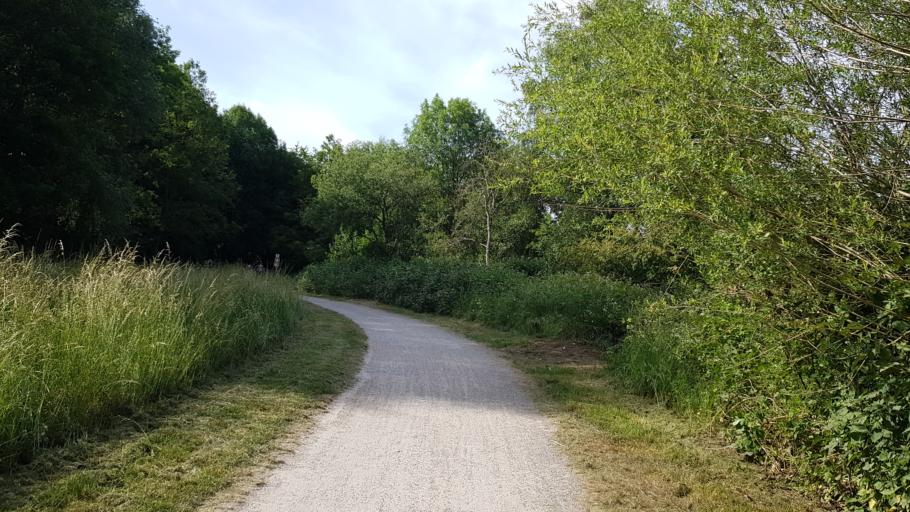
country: DE
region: North Rhine-Westphalia
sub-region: Regierungsbezirk Dusseldorf
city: Muelheim (Ruhr)
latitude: 51.4162
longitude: 6.8717
